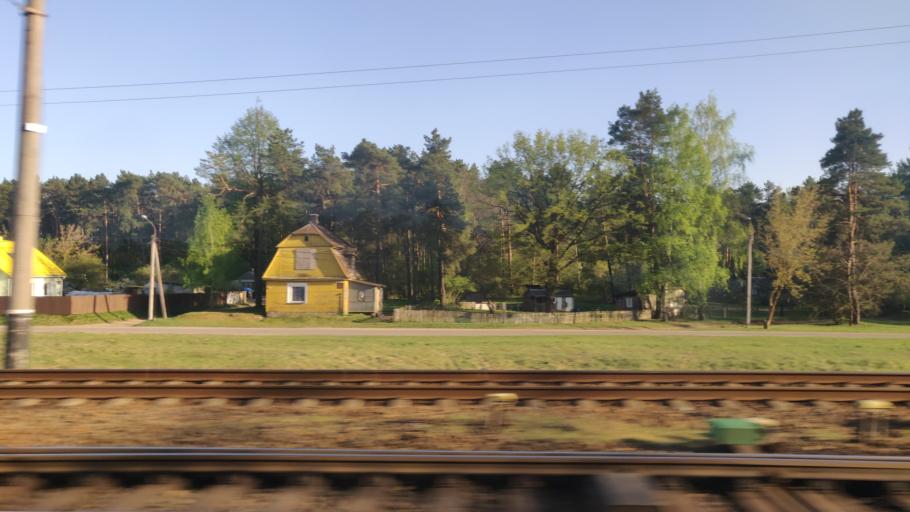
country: LT
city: Baltoji Voke
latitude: 54.6292
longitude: 25.1725
